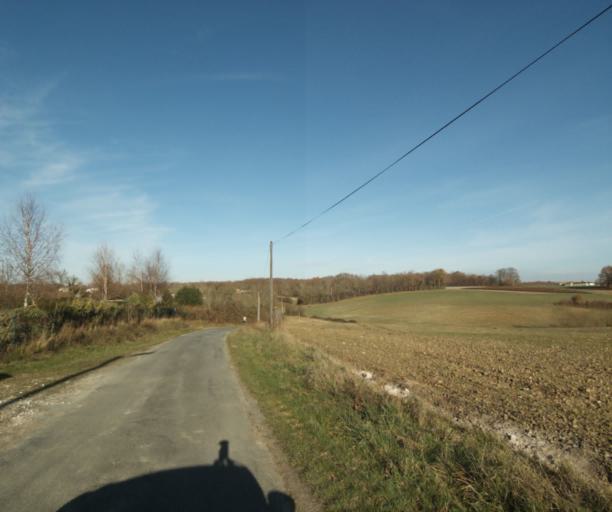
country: FR
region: Poitou-Charentes
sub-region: Departement de la Charente-Maritime
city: Ecoyeux
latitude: 45.7828
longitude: -0.5046
